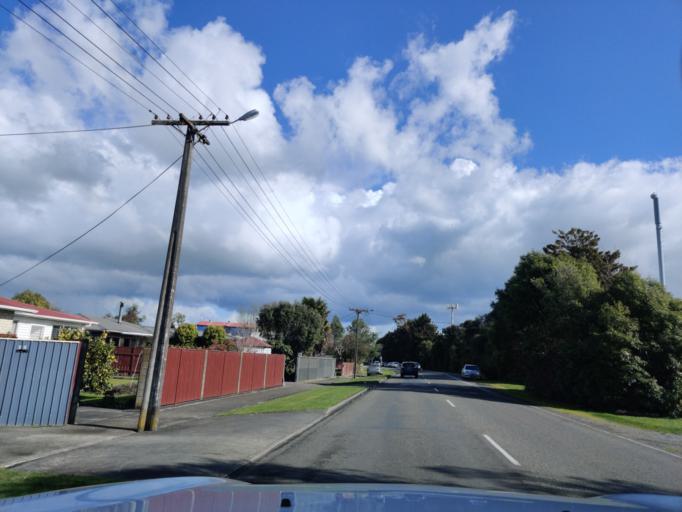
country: NZ
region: Manawatu-Wanganui
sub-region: Palmerston North City
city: Palmerston North
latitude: -40.2970
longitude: 175.7520
